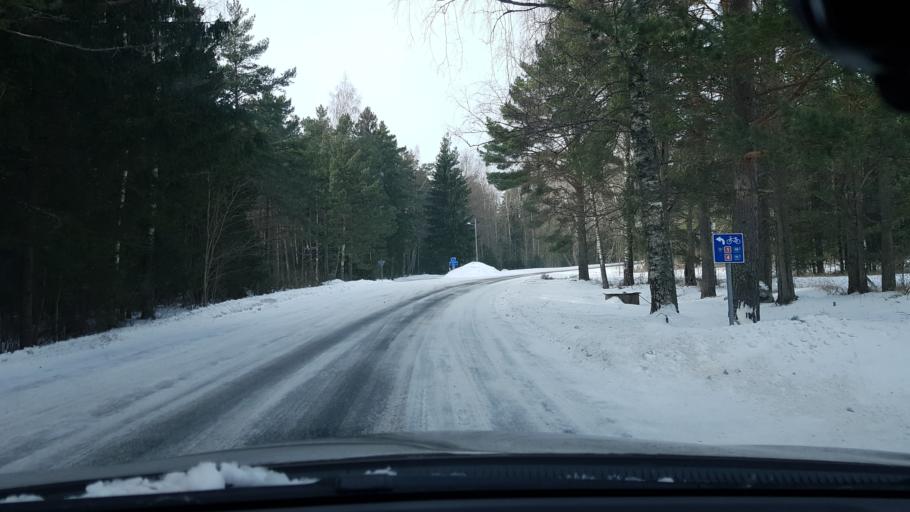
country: EE
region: Harju
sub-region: Kuusalu vald
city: Kuusalu
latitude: 59.5617
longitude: 25.5372
